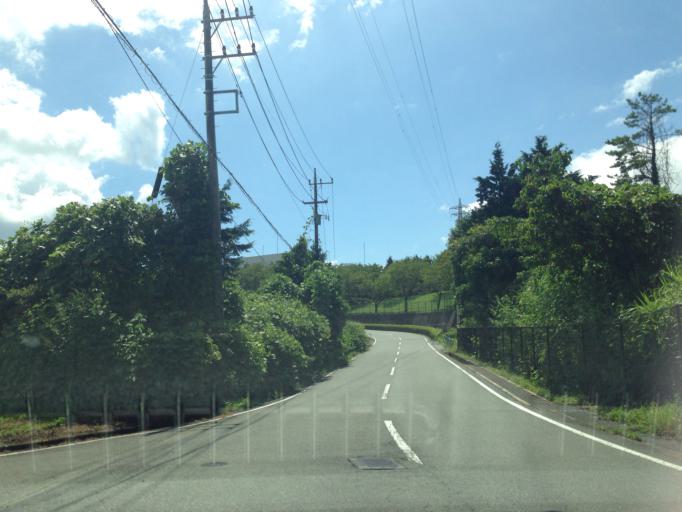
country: JP
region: Shizuoka
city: Gotemba
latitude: 35.2416
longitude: 138.8835
